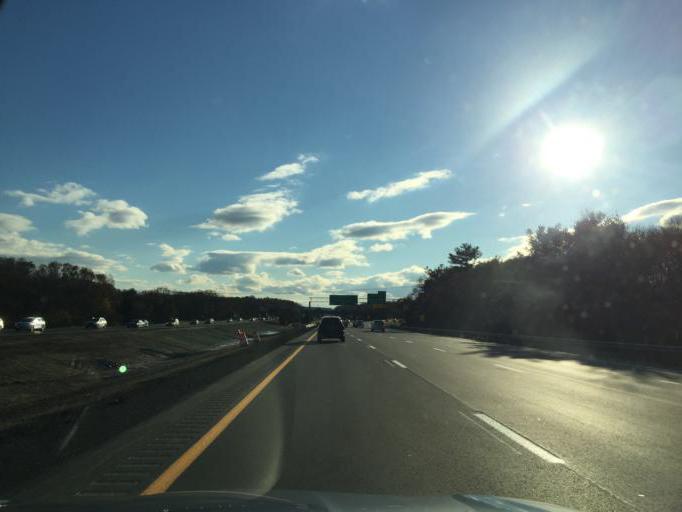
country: US
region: Massachusetts
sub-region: Bristol County
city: Attleboro
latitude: 41.9602
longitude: -71.3011
